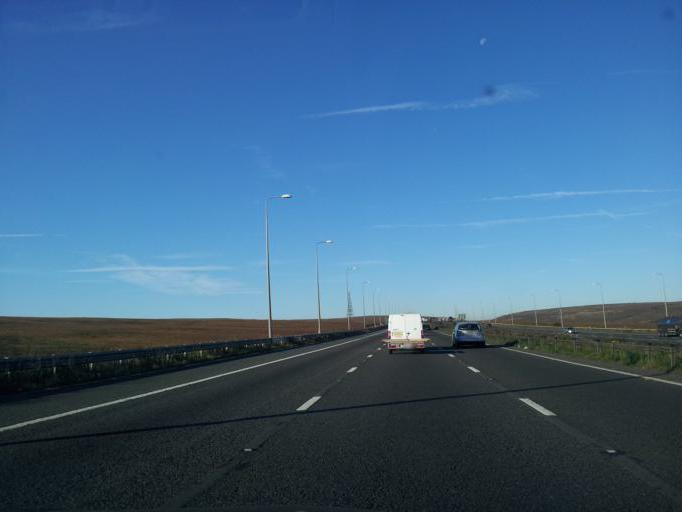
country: GB
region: England
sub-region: Borough of Oldham
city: Diggle
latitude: 53.6318
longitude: -2.0023
